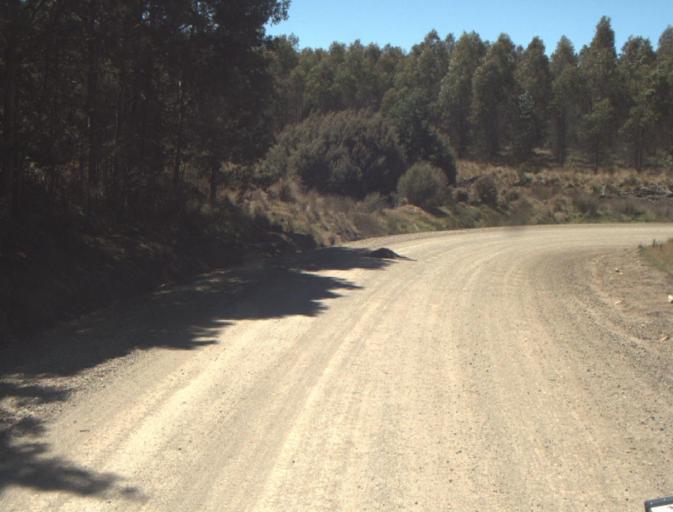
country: AU
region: Tasmania
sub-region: Dorset
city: Scottsdale
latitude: -41.3203
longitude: 147.4545
